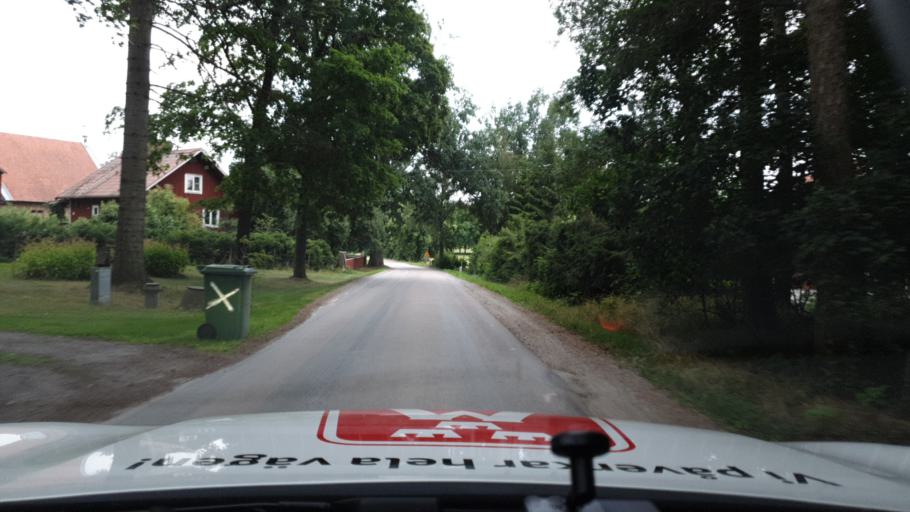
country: SE
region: Vaestmanland
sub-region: Vasteras
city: Vasteras
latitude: 59.5582
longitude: 16.6621
